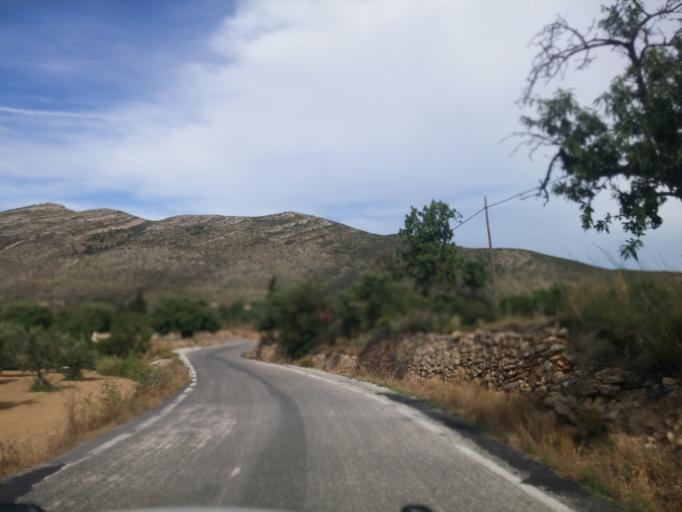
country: ES
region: Valencia
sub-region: Provincia de Alicante
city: Benissa
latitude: 38.7070
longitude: 0.0228
